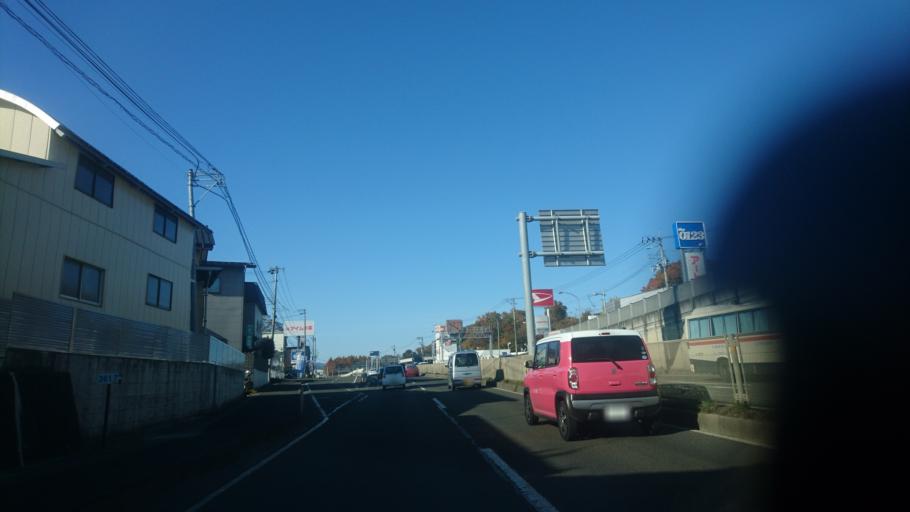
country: JP
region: Miyagi
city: Tomiya
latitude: 38.3382
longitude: 140.8854
